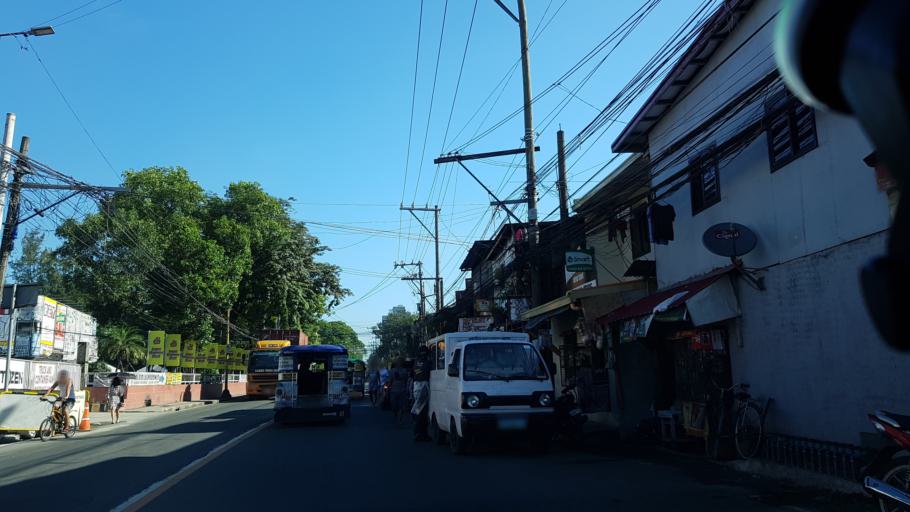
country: PH
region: Metro Manila
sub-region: Pasig
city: Pasig City
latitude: 14.5873
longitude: 121.0887
